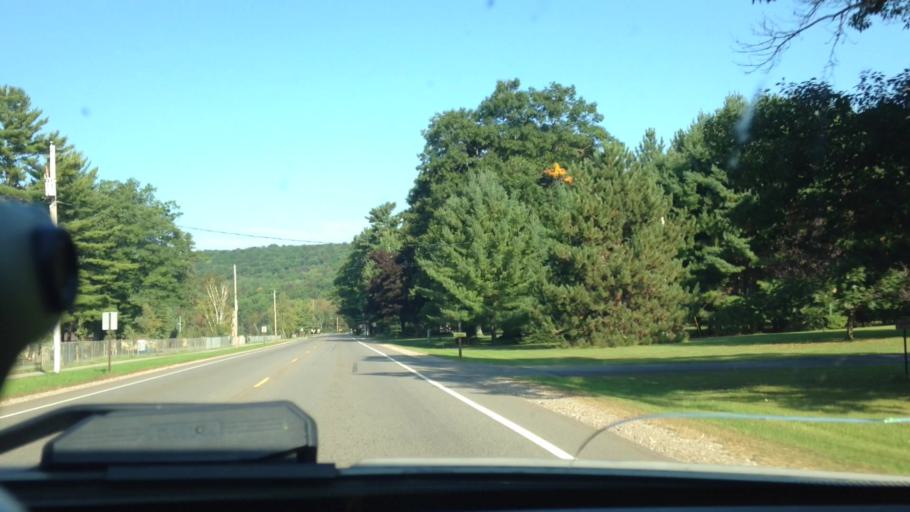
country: US
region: Michigan
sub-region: Dickinson County
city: Quinnesec
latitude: 45.8401
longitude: -88.0139
